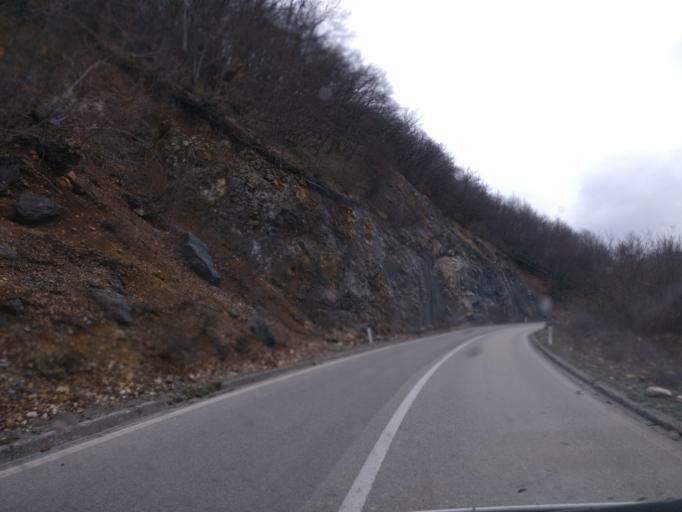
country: ME
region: Opstina Pluzine
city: Pluzine
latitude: 43.1286
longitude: 18.8149
